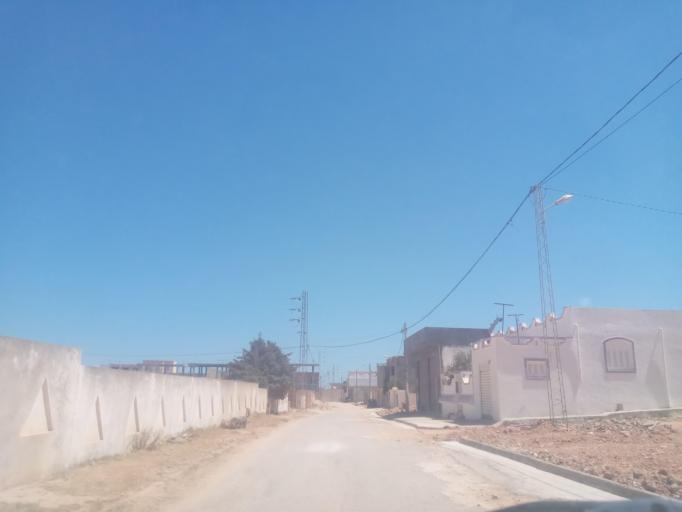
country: TN
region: Nabul
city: El Haouaria
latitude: 37.0560
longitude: 11.0048
